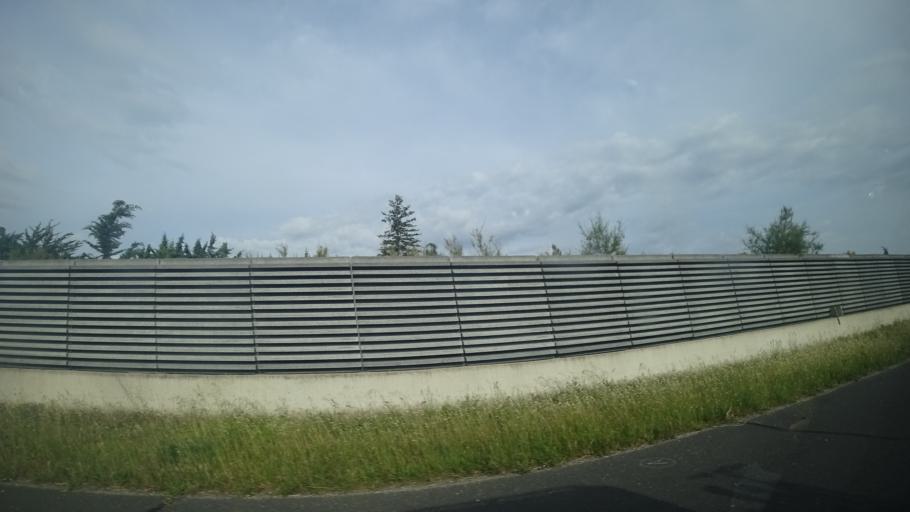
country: FR
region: Languedoc-Roussillon
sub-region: Departement de l'Herault
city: Lezignan-la-Cebe
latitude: 43.4817
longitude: 3.4377
